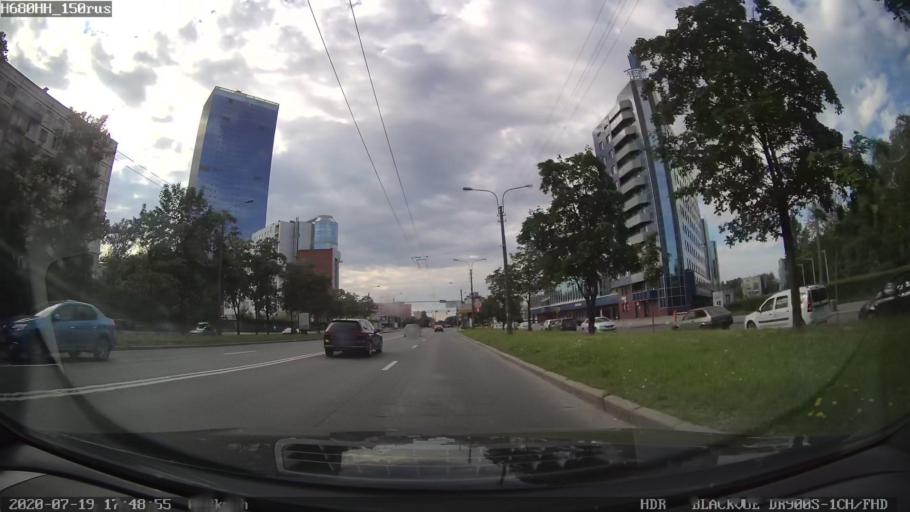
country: RU
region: St.-Petersburg
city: Kupchino
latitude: 59.8498
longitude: 30.3090
